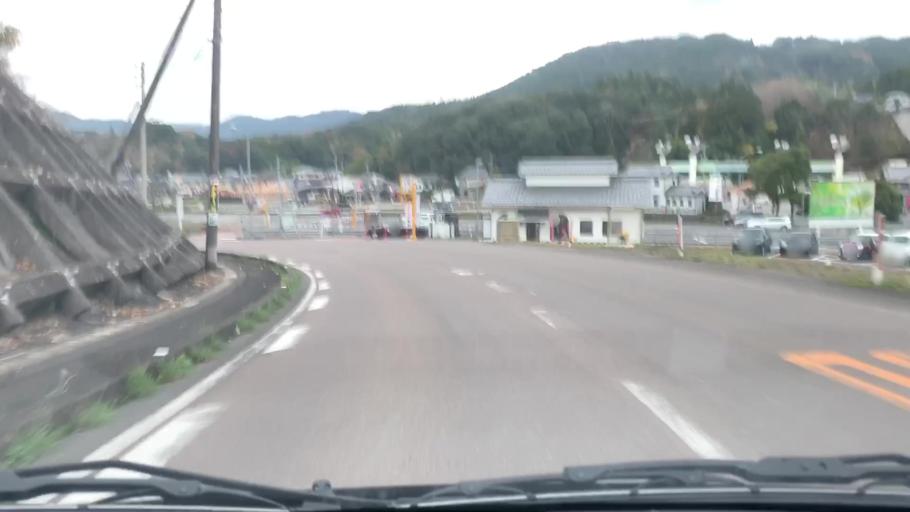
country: JP
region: Saga Prefecture
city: Ureshinomachi-shimojuku
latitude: 33.1094
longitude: 129.9761
